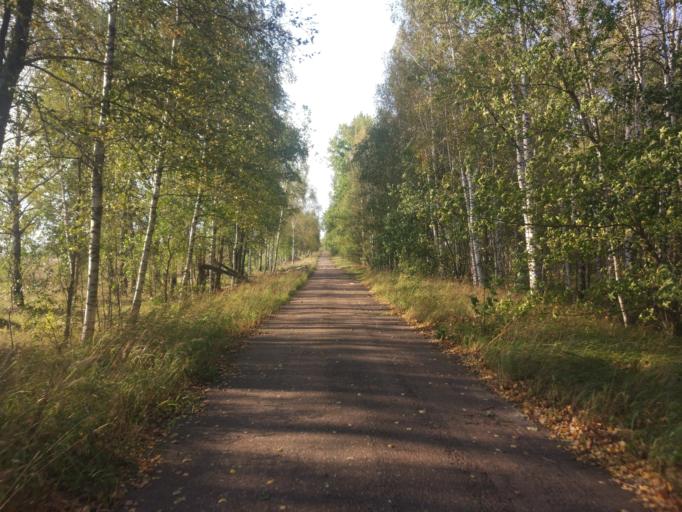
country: RU
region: Brjansk
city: Vyshkov
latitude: 52.6588
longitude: 31.5797
